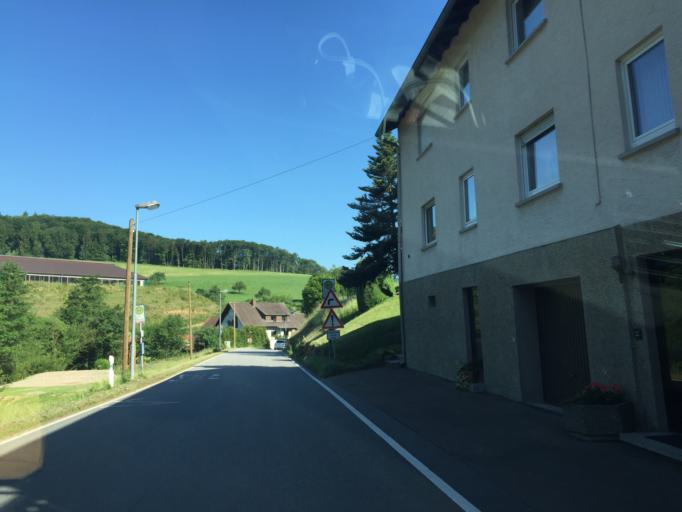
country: DE
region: Hesse
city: Unter-Abtsteinach
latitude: 49.5214
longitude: 8.7461
